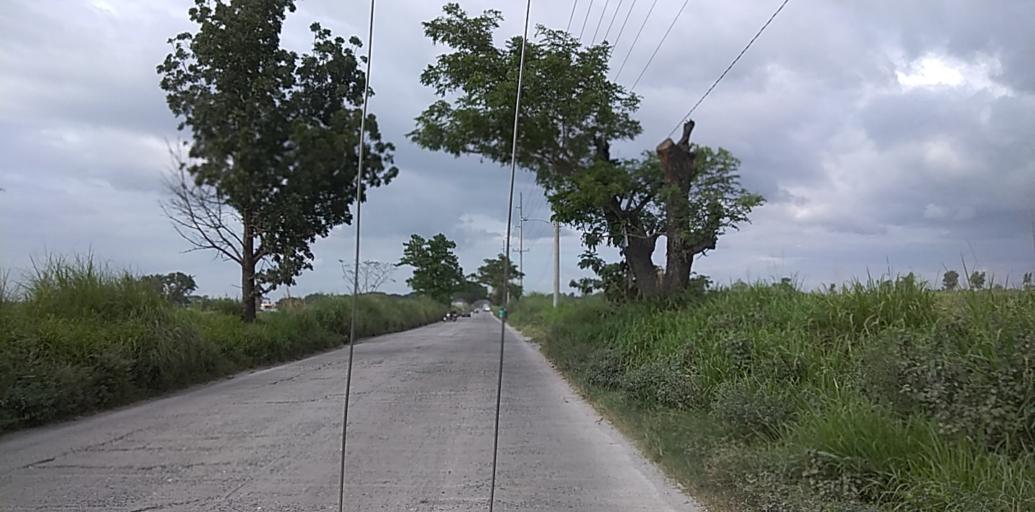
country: PH
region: Central Luzon
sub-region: Province of Pampanga
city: Porac
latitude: 15.0712
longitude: 120.5500
